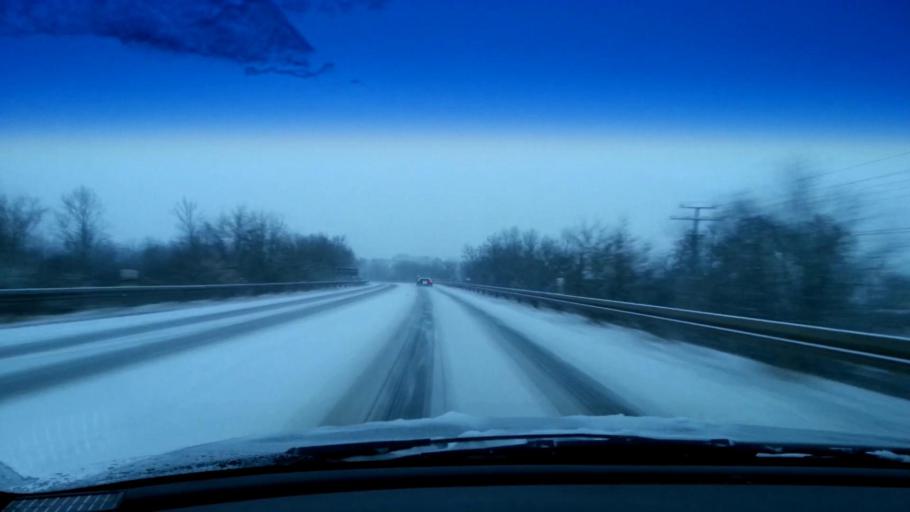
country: DE
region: Bavaria
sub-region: Upper Franconia
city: Hallstadt
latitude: 49.9266
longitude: 10.8987
